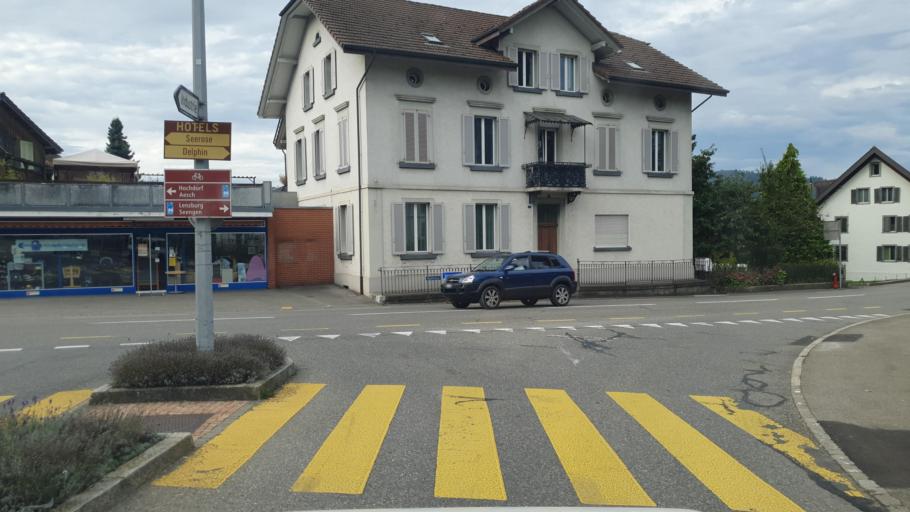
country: CH
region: Aargau
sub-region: Bezirk Lenzburg
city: Meisterschwanden
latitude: 47.2950
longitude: 8.2292
